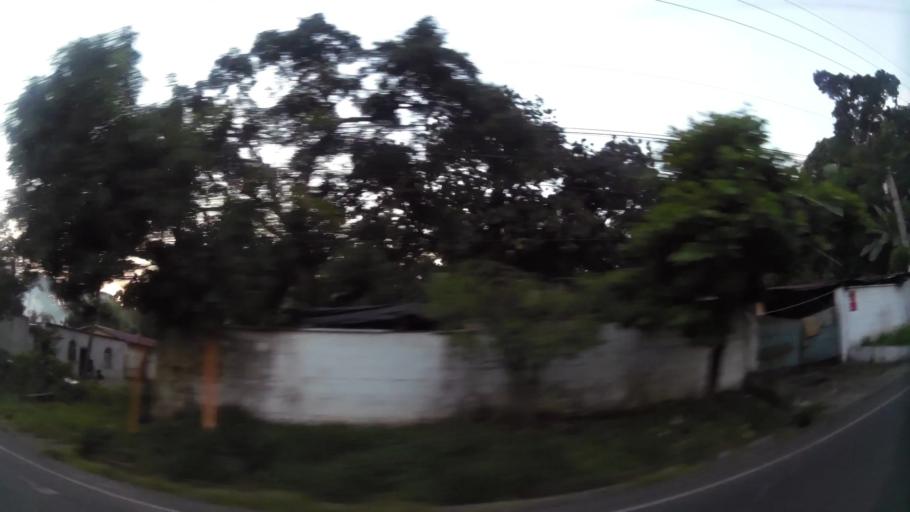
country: GT
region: Retalhuleu
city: Santa Cruz Mulua
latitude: 14.5882
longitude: -91.6214
